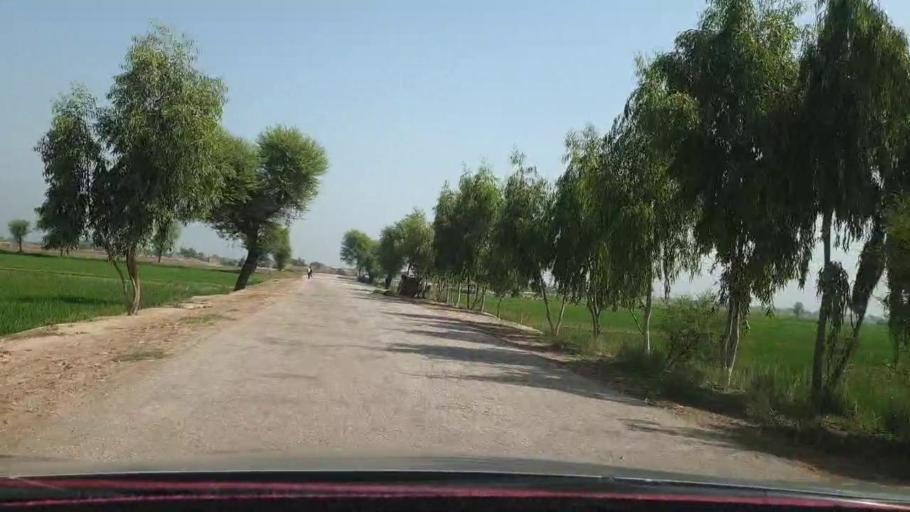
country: PK
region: Sindh
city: Warah
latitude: 27.4730
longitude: 67.8318
